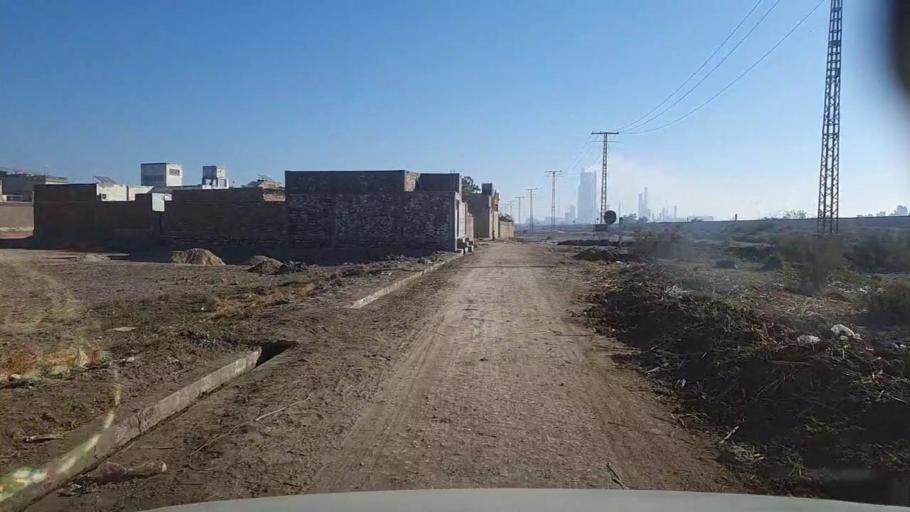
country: PK
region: Sindh
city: Khairpur
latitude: 28.0396
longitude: 69.6553
